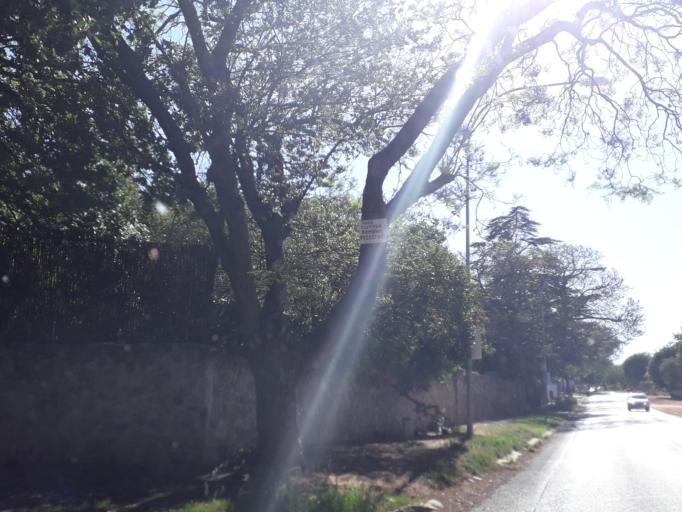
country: ZA
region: Gauteng
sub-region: City of Johannesburg Metropolitan Municipality
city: Roodepoort
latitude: -26.1363
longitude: 27.9644
